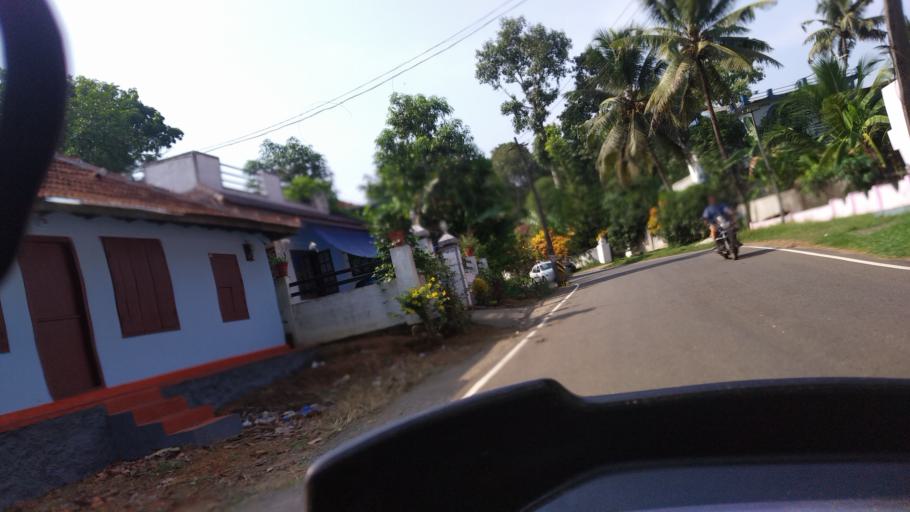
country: IN
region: Kerala
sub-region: Ernakulam
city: Piravam
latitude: 9.8249
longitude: 76.5483
